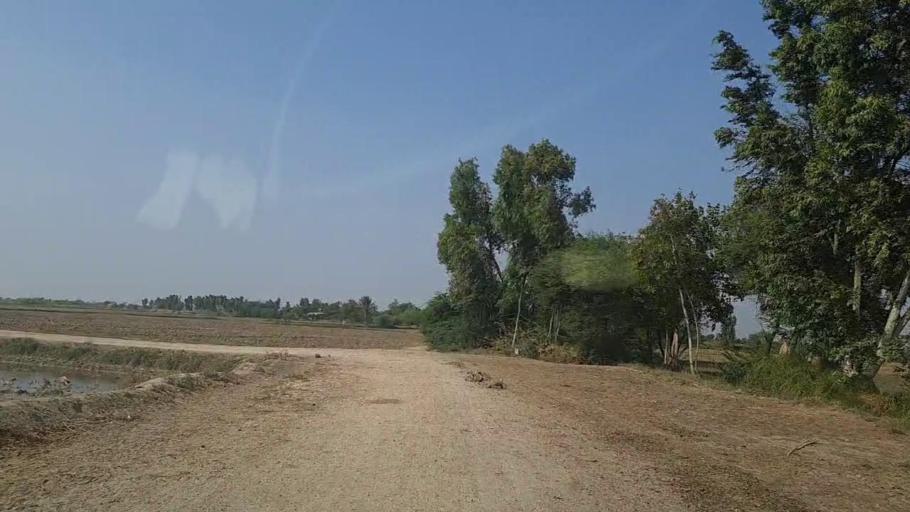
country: PK
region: Sindh
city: Mirpur Sakro
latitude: 24.5673
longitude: 67.8262
